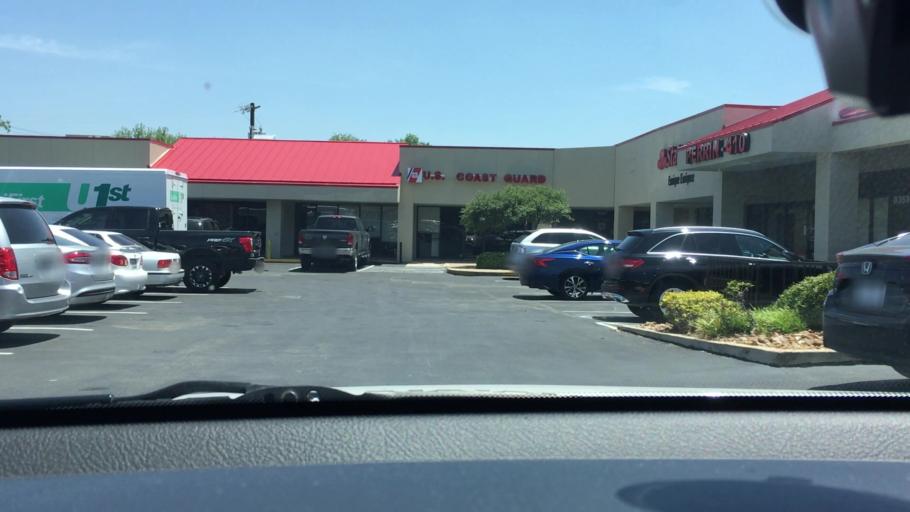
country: US
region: Texas
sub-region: Bexar County
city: Windcrest
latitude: 29.5146
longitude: -98.4113
